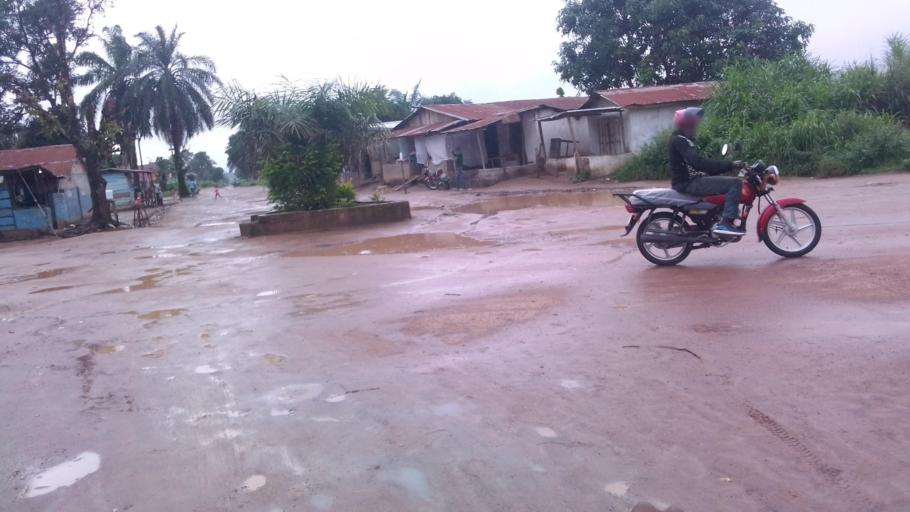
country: SL
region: Eastern Province
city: Kenema
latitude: 7.8963
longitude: -11.1730
